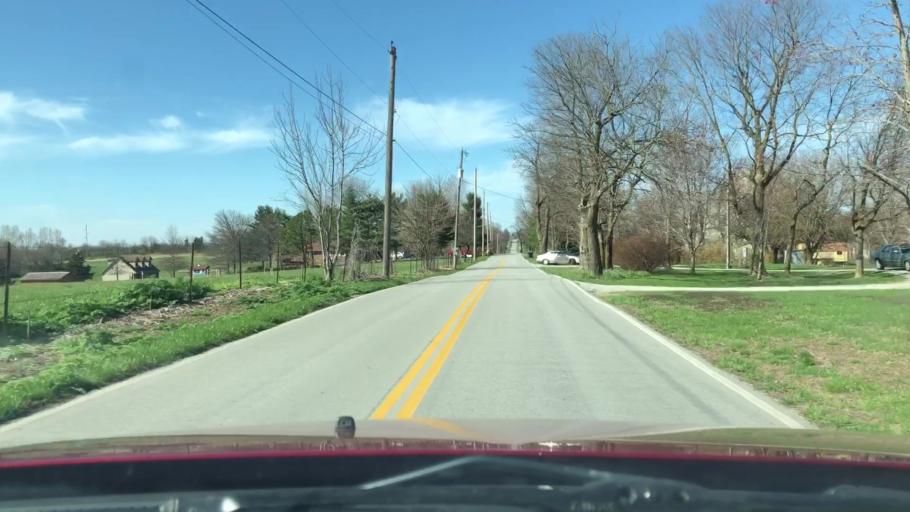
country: US
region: Missouri
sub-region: Greene County
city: Strafford
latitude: 37.2259
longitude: -93.1884
